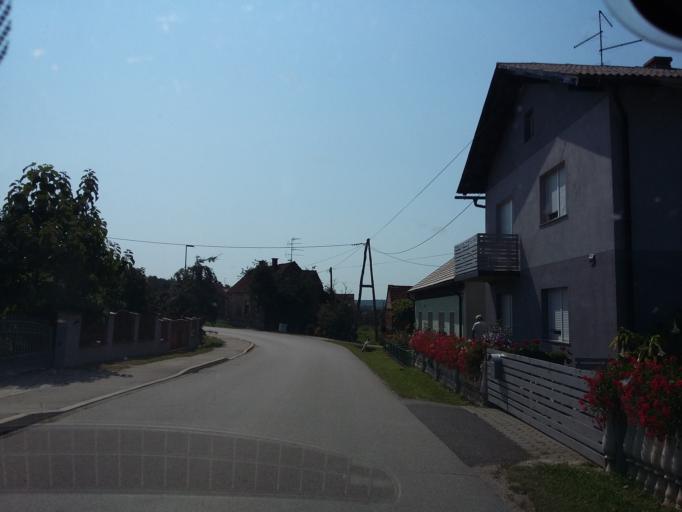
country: SI
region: Hodos-Hodos
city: Hodos
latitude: 46.8326
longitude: 16.3192
